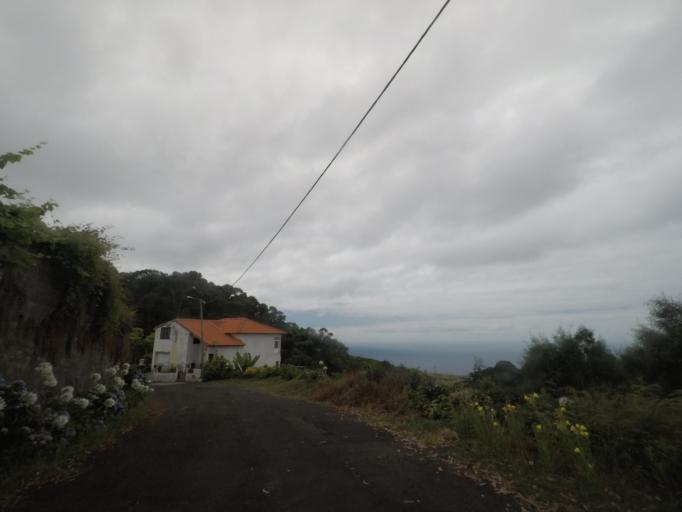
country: PT
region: Madeira
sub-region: Porto Moniz
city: Porto Moniz
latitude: 32.8635
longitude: -17.1875
